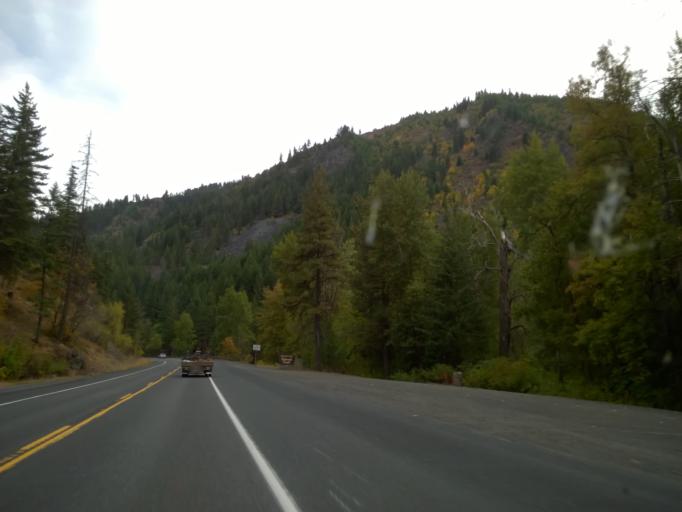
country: US
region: Washington
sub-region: Chelan County
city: Leavenworth
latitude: 47.4629
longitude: -120.6602
